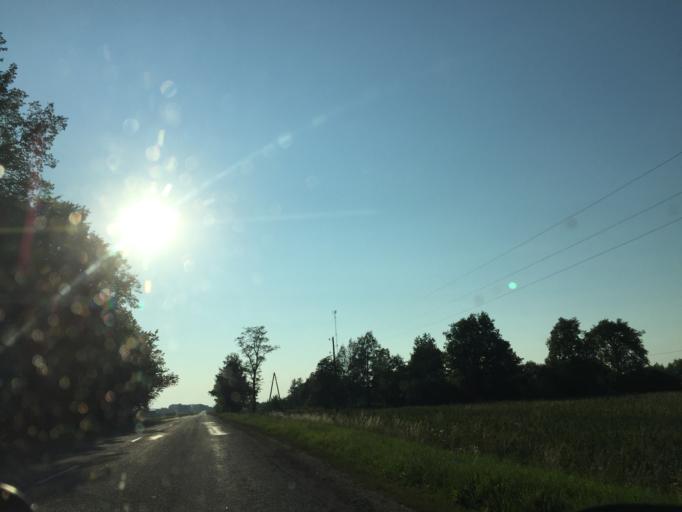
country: LV
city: Tervete
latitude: 56.4370
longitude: 23.5114
